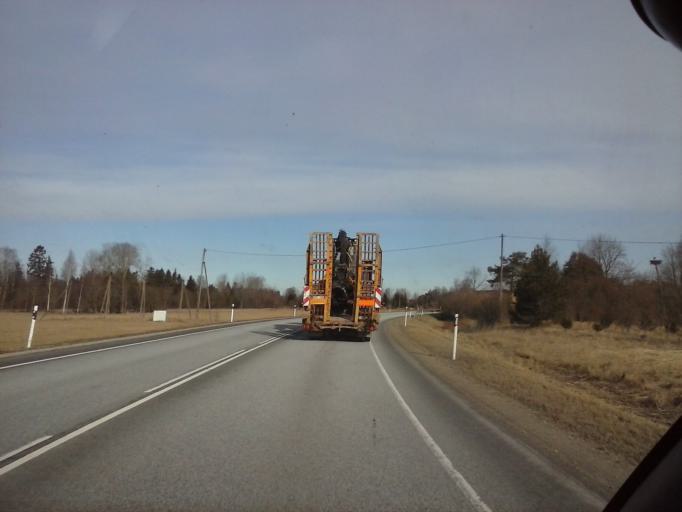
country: EE
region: Jaervamaa
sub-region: Paide linn
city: Paide
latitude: 58.8689
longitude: 25.7041
